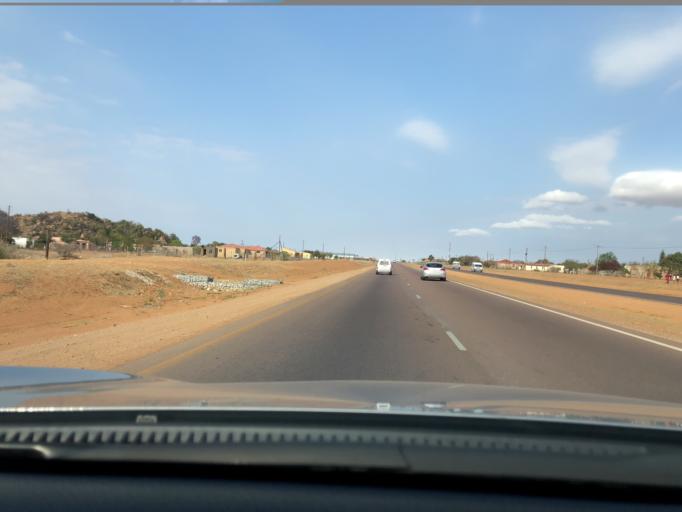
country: ZA
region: Limpopo
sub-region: Capricorn District Municipality
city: Mankoeng
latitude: -23.8912
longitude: 29.6574
